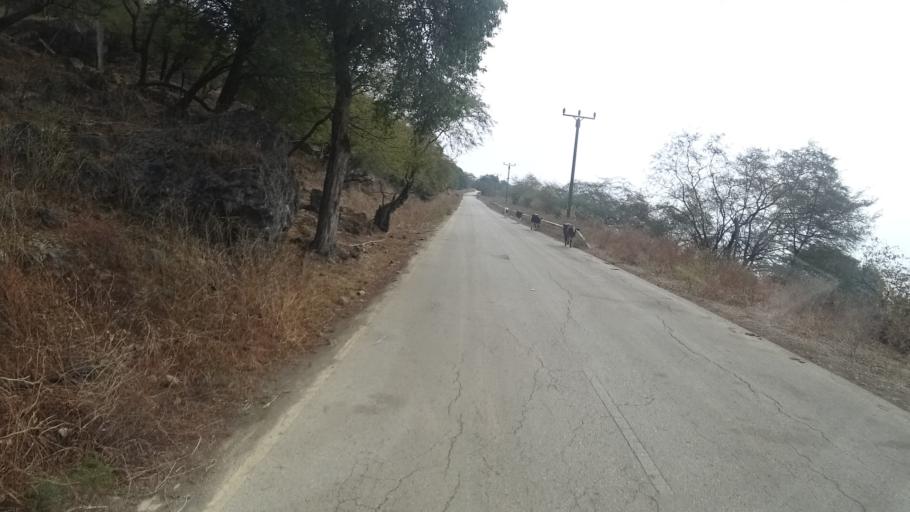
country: YE
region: Al Mahrah
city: Hawf
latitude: 16.7116
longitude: 53.2310
